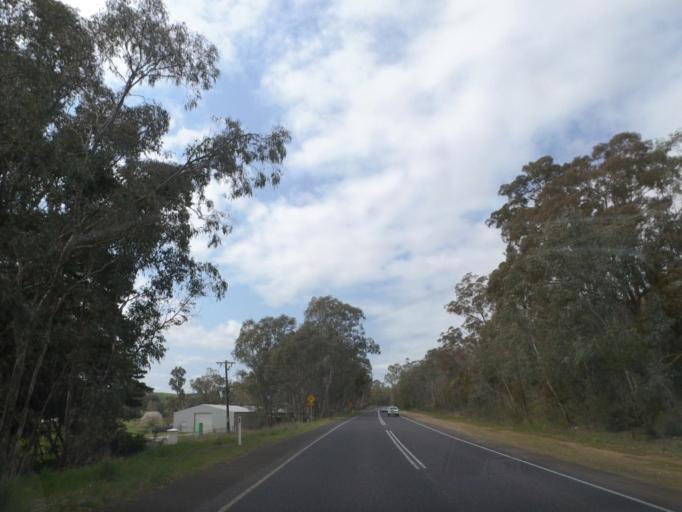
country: AU
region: Victoria
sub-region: Murrindindi
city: Kinglake West
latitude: -37.1402
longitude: 145.2627
